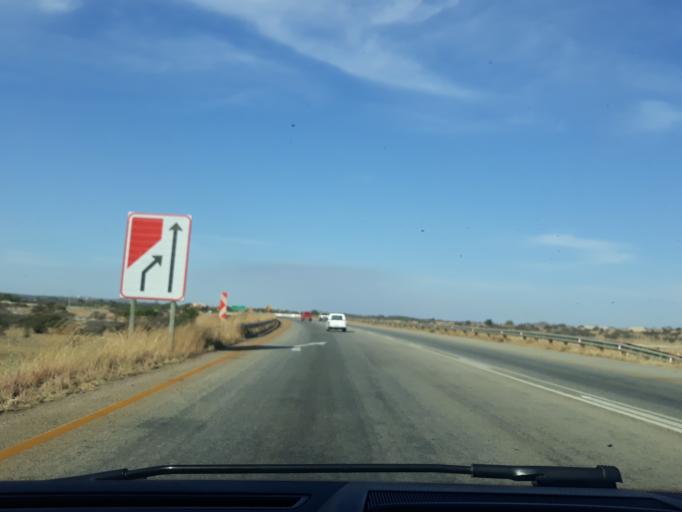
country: ZA
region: Limpopo
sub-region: Capricorn District Municipality
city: Polokwane
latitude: -23.9467
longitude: 29.4123
